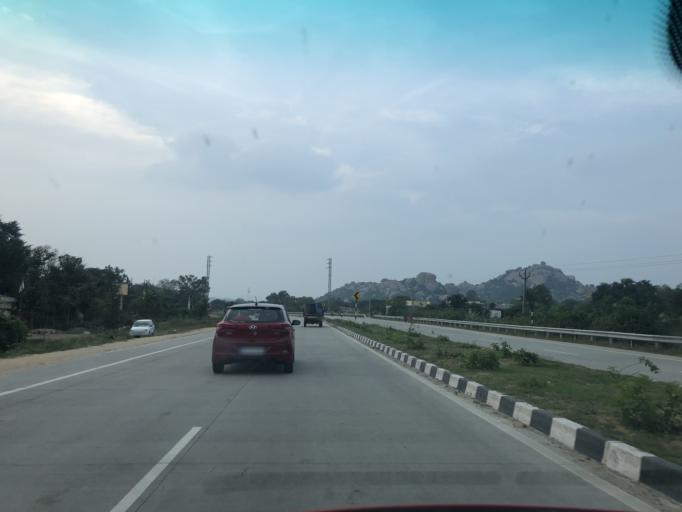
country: IN
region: Andhra Pradesh
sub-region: Chittoor
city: Chittoor
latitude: 13.1972
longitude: 79.0002
